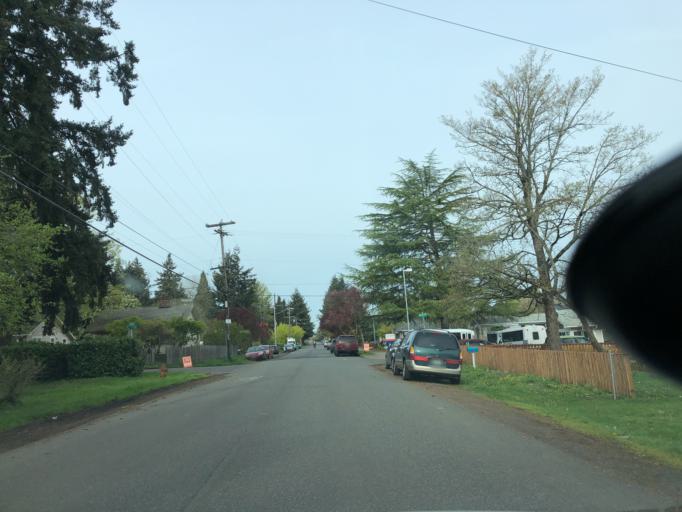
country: US
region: Oregon
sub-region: Multnomah County
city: Portland
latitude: 45.5591
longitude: -122.6039
